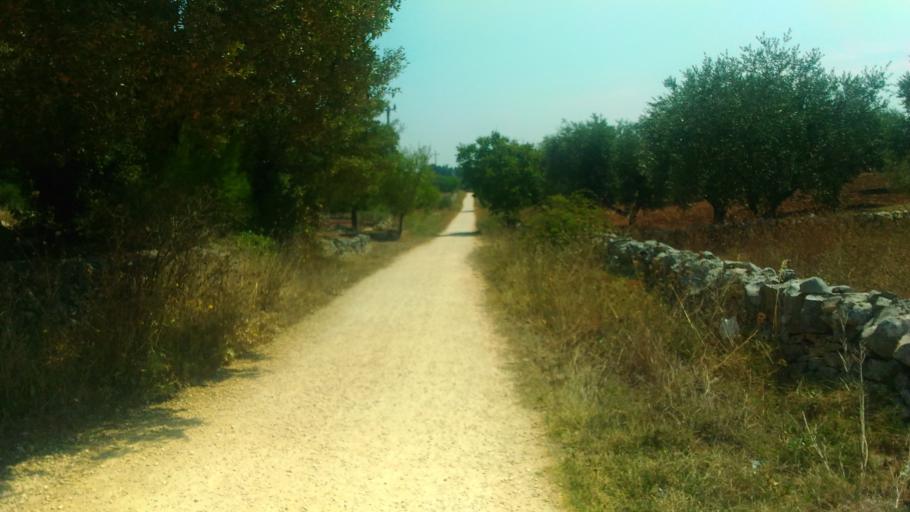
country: IT
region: Apulia
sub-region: Provincia di Brindisi
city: Cisternino
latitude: 40.7274
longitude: 17.3936
